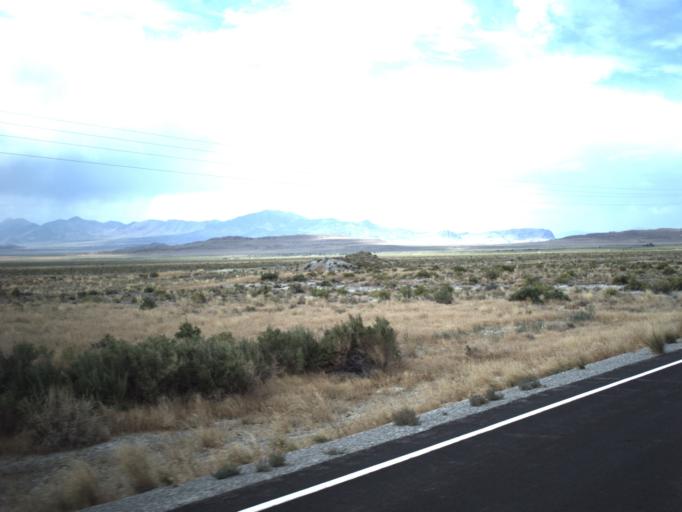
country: US
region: Utah
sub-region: Tooele County
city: Wendover
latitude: 41.4281
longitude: -113.8268
